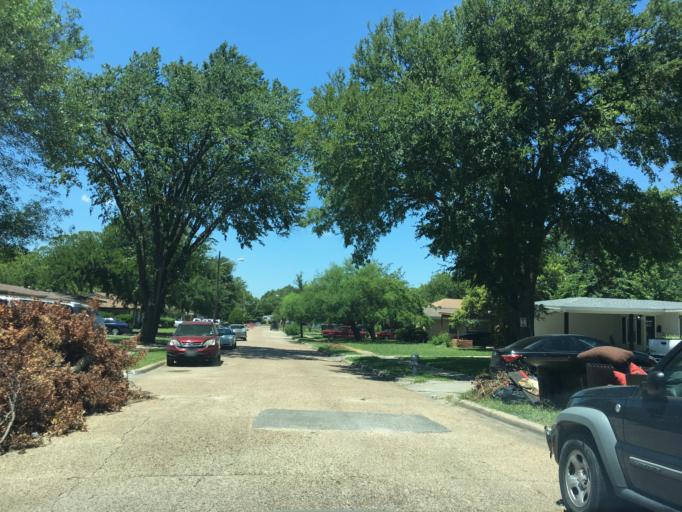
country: US
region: Texas
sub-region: Dallas County
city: Garland
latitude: 32.8516
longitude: -96.6743
